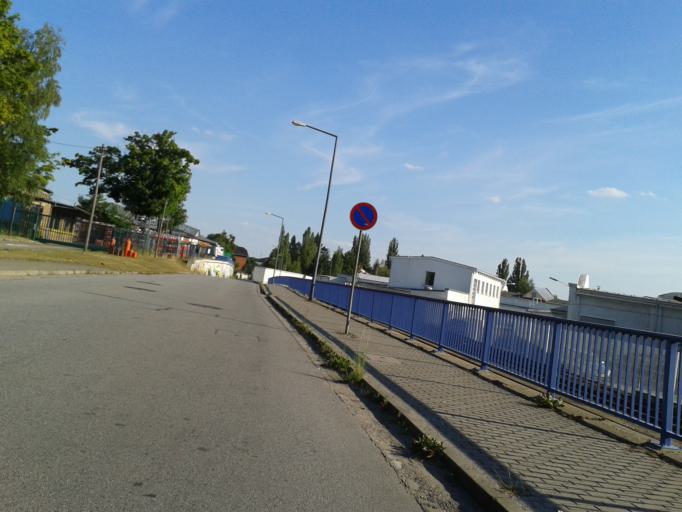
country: DE
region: Saxony
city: Albertstadt
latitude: 51.0875
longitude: 13.7677
